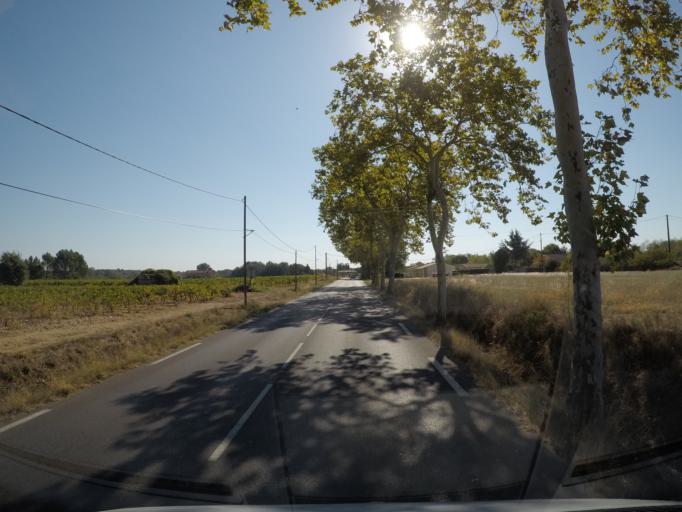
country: FR
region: Languedoc-Roussillon
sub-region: Departement du Gard
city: Boisset-et-Gaujac
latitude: 44.0345
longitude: 4.0064
